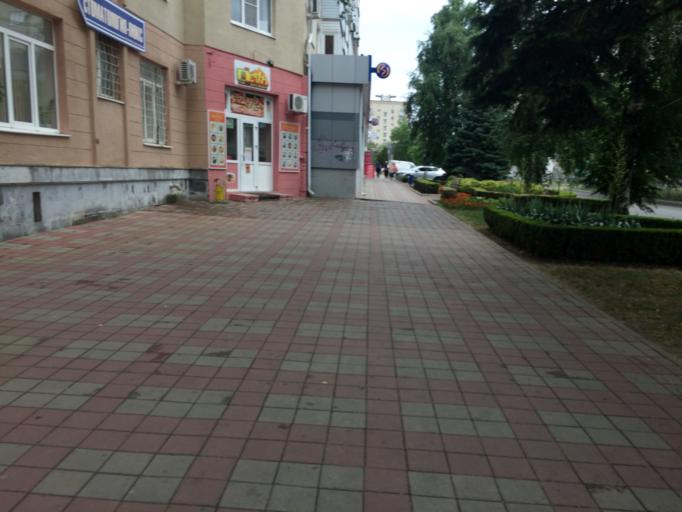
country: RU
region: Stavropol'skiy
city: Stavropol'
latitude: 45.0395
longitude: 41.9705
